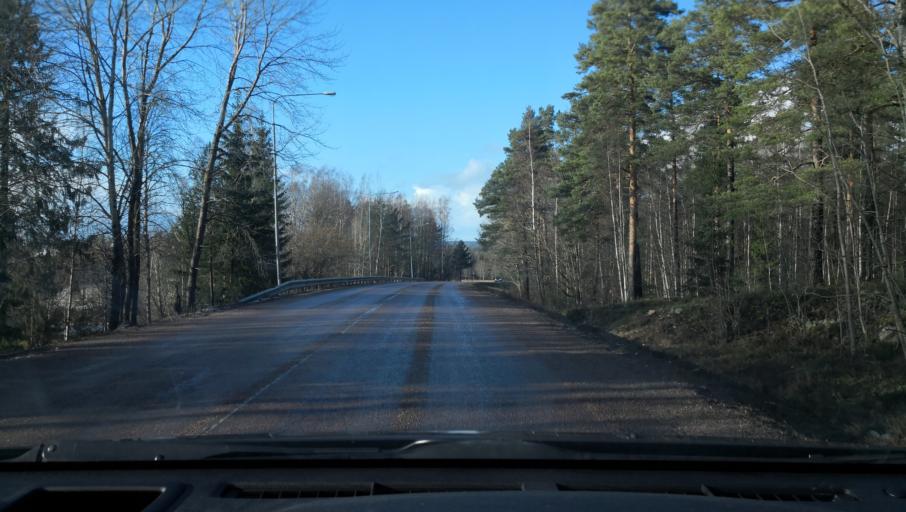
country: SE
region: Vaestmanland
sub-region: Arboga Kommun
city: Arboga
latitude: 59.3789
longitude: 15.8402
